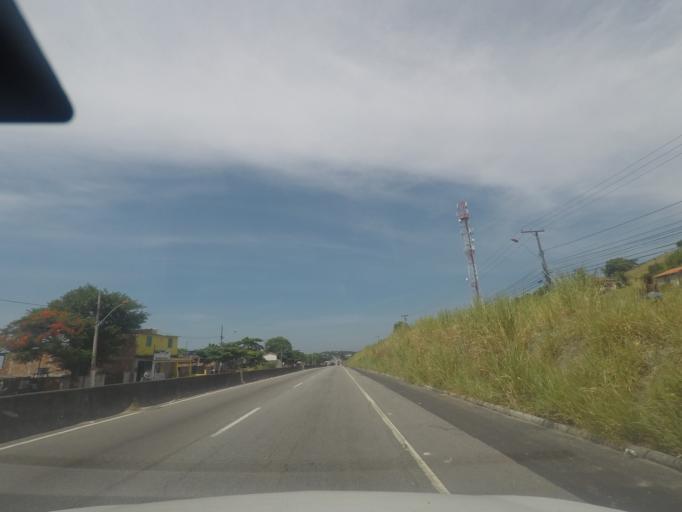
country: BR
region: Rio de Janeiro
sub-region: Marica
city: Marica
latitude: -22.9216
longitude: -42.8583
